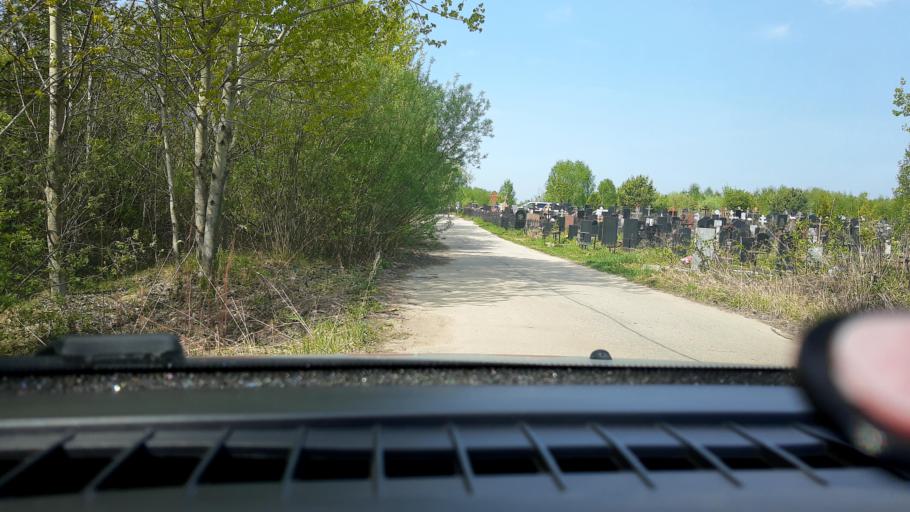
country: RU
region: Nizjnij Novgorod
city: Gorbatovka
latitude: 56.2267
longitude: 43.7562
